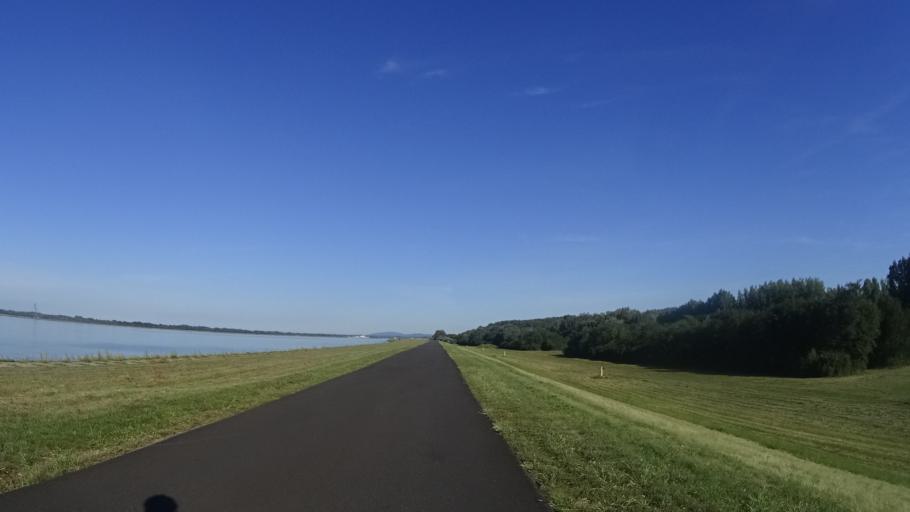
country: SK
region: Trnavsky
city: Samorin
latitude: 48.0228
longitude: 17.2749
